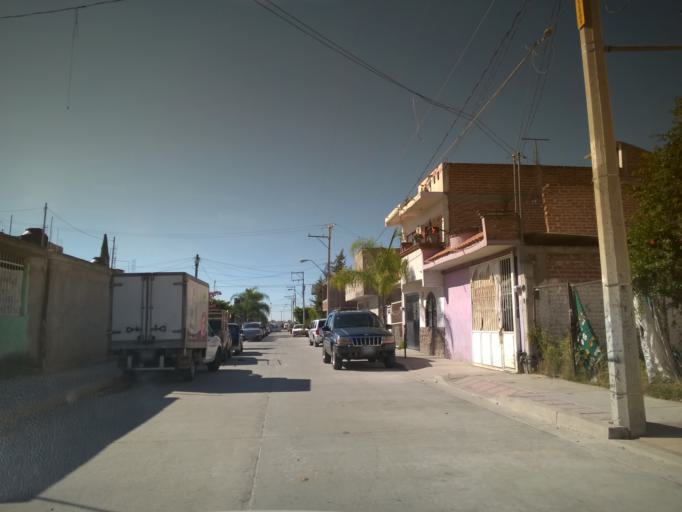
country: MX
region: Guanajuato
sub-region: Leon
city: San Jose de Duran (Los Troncoso)
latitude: 21.0693
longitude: -101.6360
